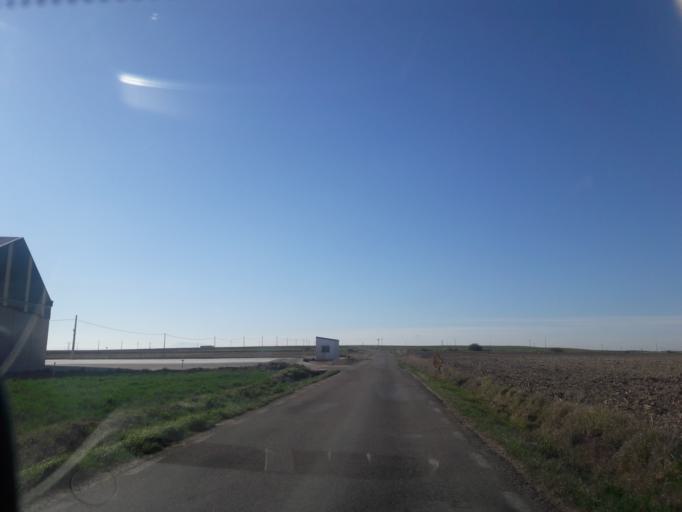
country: ES
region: Castille and Leon
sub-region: Provincia de Salamanca
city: Penarandilla
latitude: 40.8754
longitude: -5.3902
